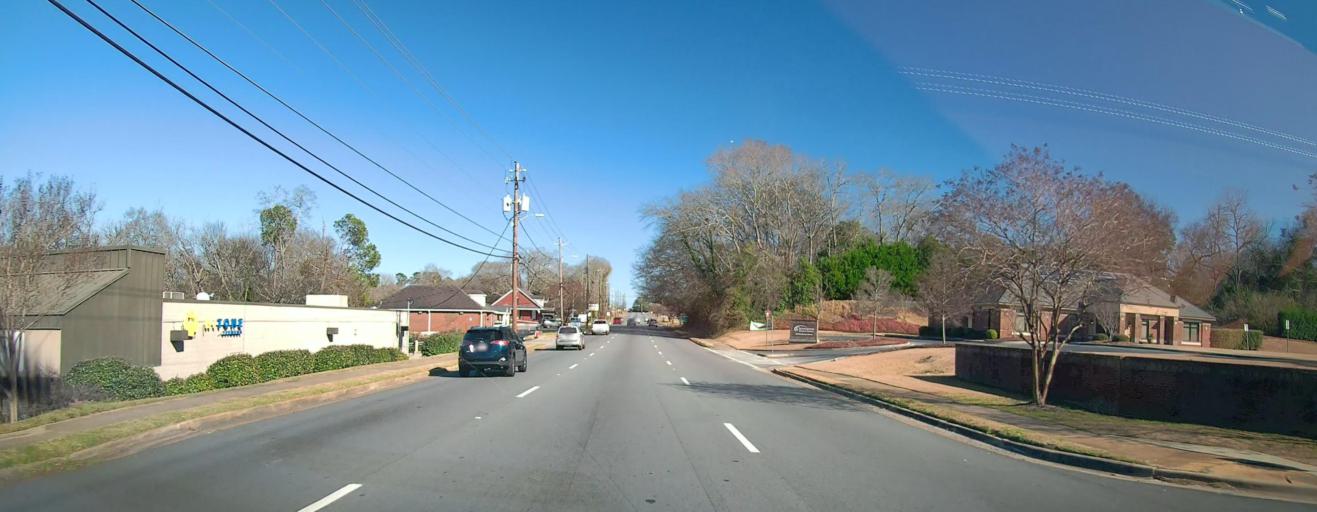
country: US
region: Georgia
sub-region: Sumter County
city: Americus
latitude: 32.0720
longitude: -84.2296
